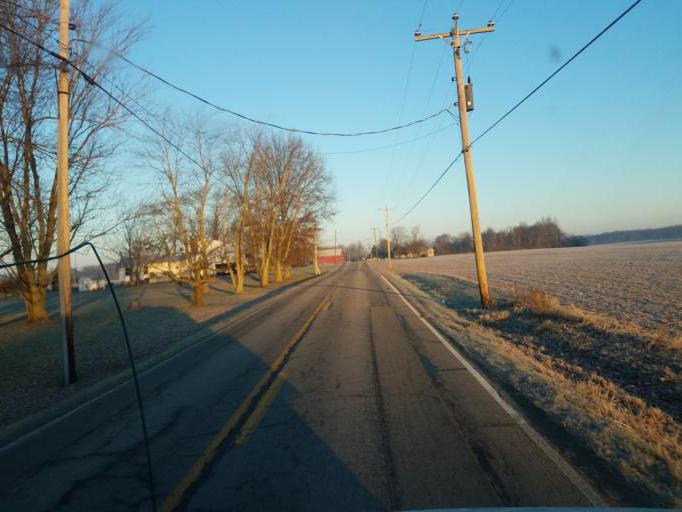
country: US
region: Ohio
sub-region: Marion County
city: Marion
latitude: 40.5302
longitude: -83.0672
